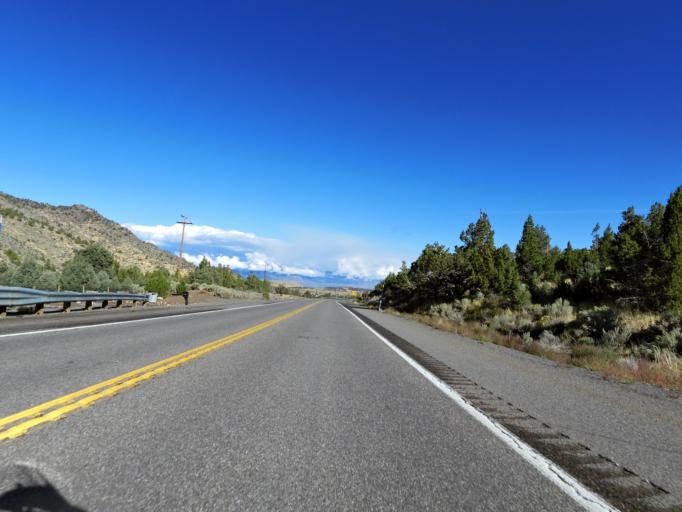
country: US
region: Nevada
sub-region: Douglas County
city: Gardnerville Ranchos
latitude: 38.8360
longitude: -119.6326
